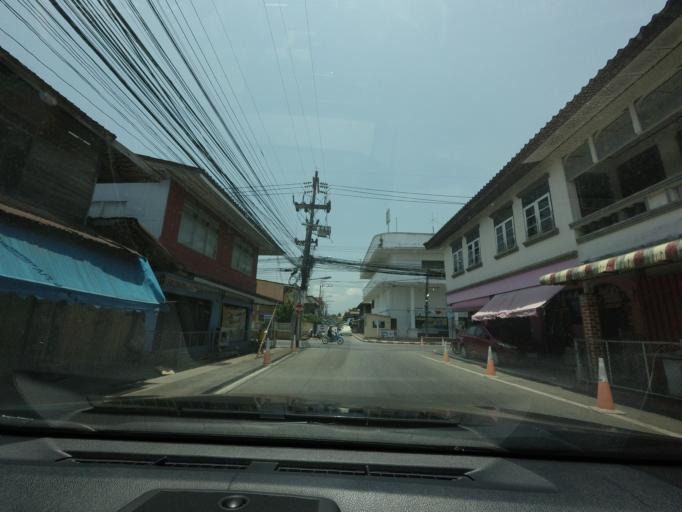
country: TH
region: Pattani
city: Yaring
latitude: 6.8656
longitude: 101.3702
